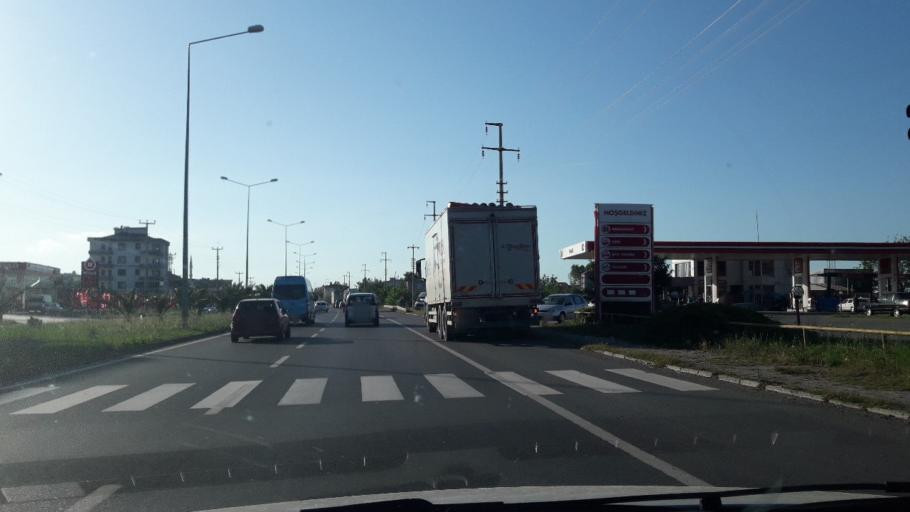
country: TR
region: Samsun
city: Taflan
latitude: 41.4156
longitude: 36.1727
